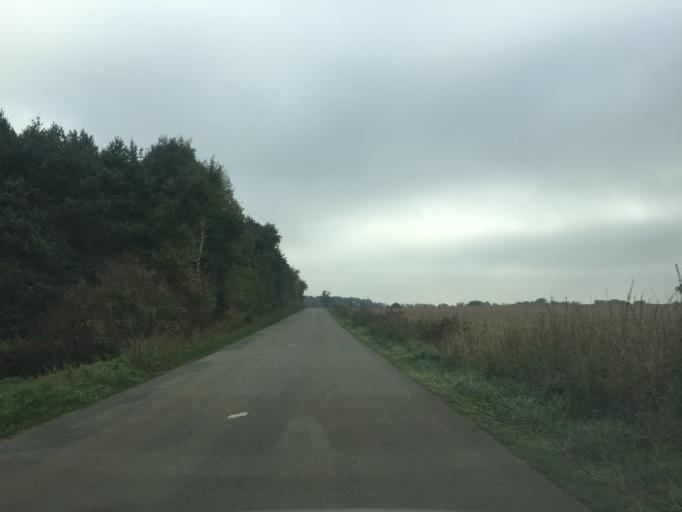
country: FR
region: Rhone-Alpes
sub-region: Departement de l'Ain
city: Saint-Andre-de-Corcy
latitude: 45.9107
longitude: 4.9574
